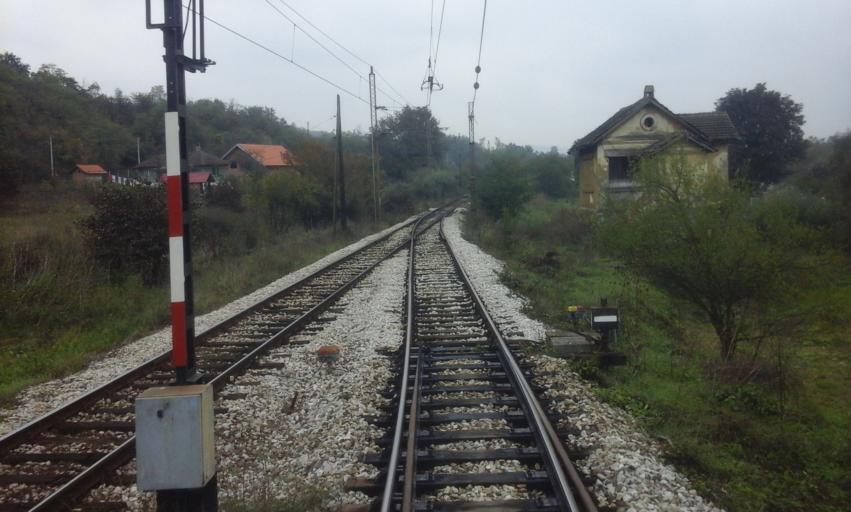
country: RS
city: Rusanj
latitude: 44.6388
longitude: 20.5330
